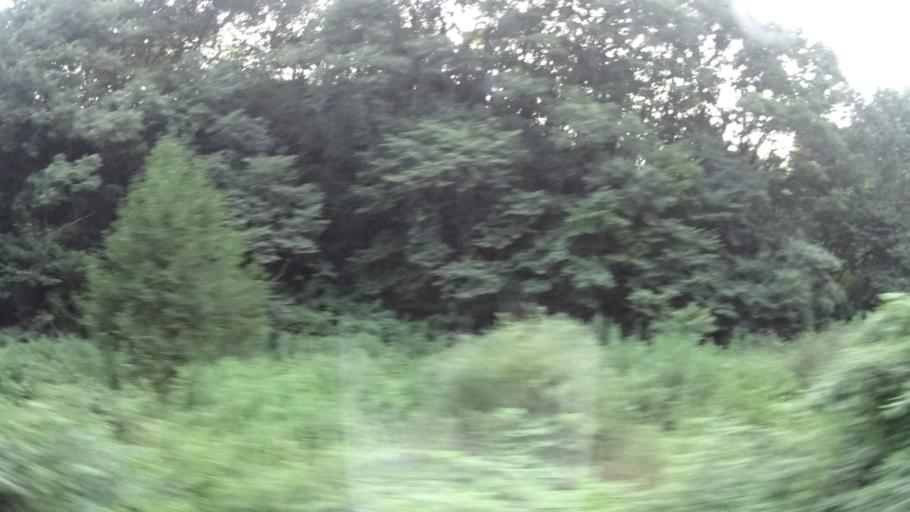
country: JP
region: Tochigi
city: Karasuyama
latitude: 36.6121
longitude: 140.1542
